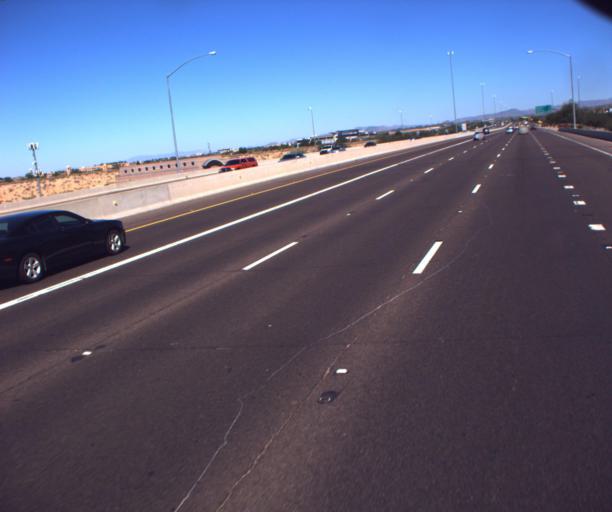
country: US
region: Arizona
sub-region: Maricopa County
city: Paradise Valley
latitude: 33.6305
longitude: -111.8902
